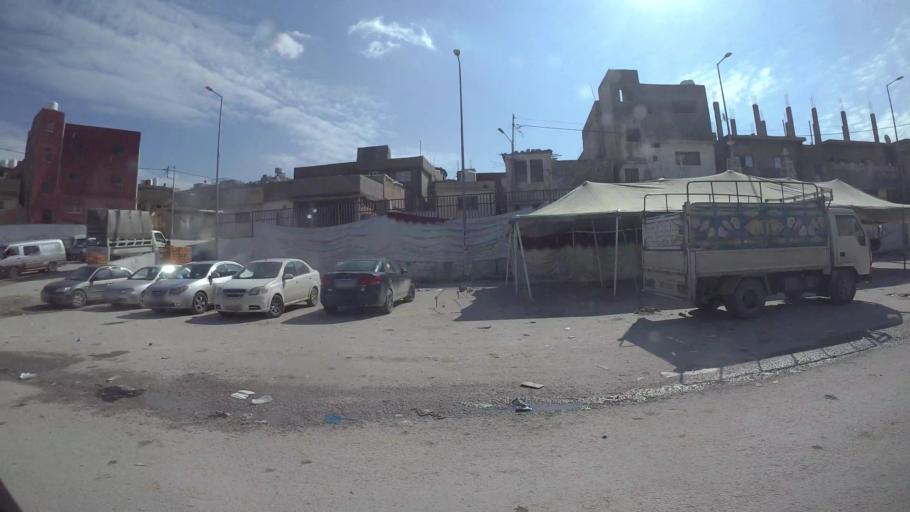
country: JO
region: Amman
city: Al Jubayhah
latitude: 32.0687
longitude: 35.8431
